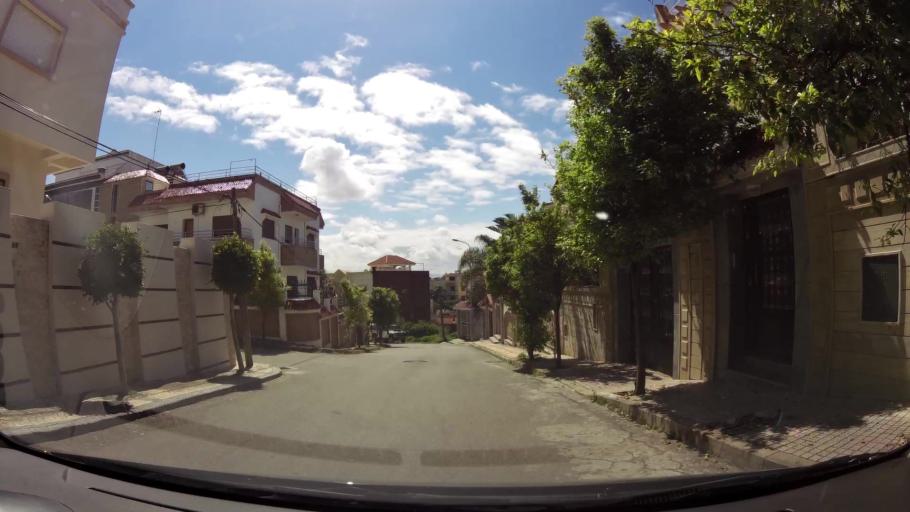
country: MA
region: Tanger-Tetouan
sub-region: Tanger-Assilah
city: Tangier
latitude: 35.7784
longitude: -5.8302
